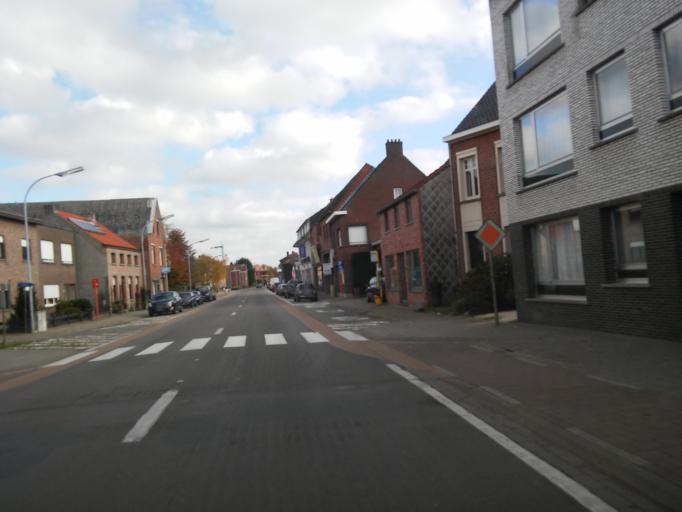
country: BE
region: Flanders
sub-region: Provincie Antwerpen
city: Berlaar
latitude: 51.1172
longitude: 4.6465
